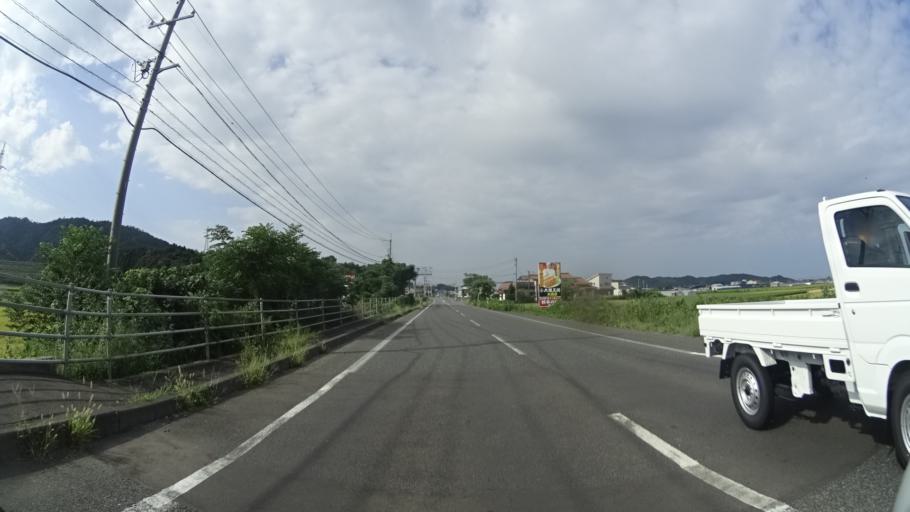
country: JP
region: Shimane
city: Odacho-oda
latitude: 35.2292
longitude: 132.5221
